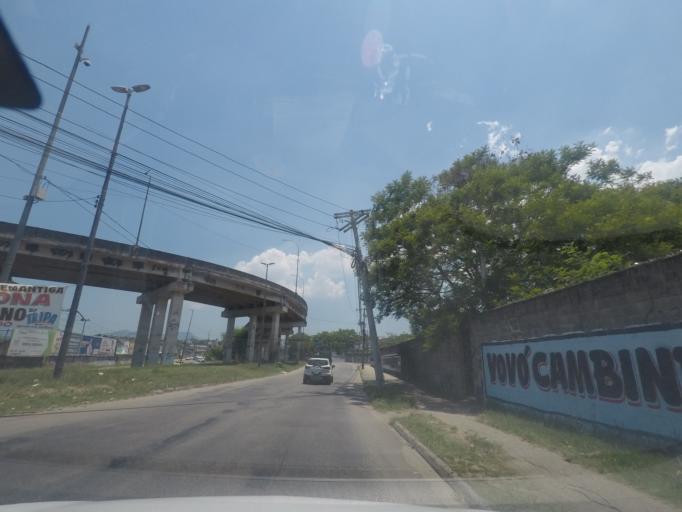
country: BR
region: Rio de Janeiro
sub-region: Duque De Caxias
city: Duque de Caxias
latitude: -22.8014
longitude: -43.3055
